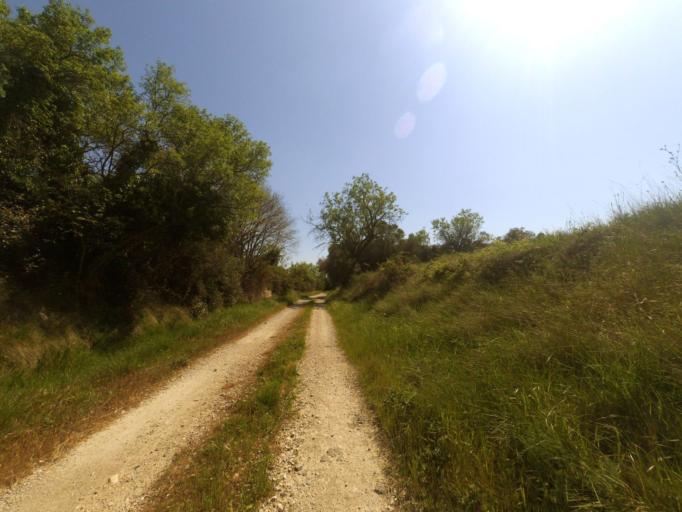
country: FR
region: Languedoc-Roussillon
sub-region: Departement du Gard
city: Congenies
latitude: 43.7773
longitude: 4.1674
